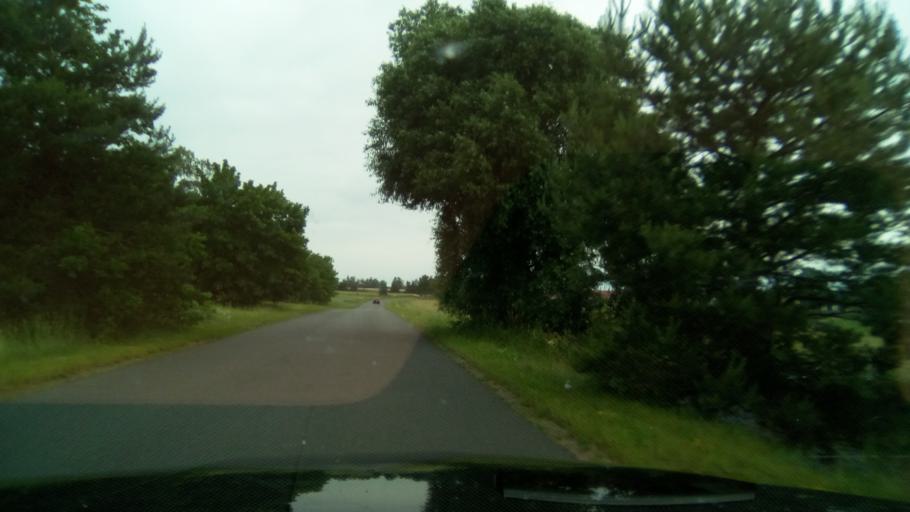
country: PL
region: Greater Poland Voivodeship
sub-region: Powiat gnieznienski
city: Czerniejewo
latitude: 52.4756
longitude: 17.5162
